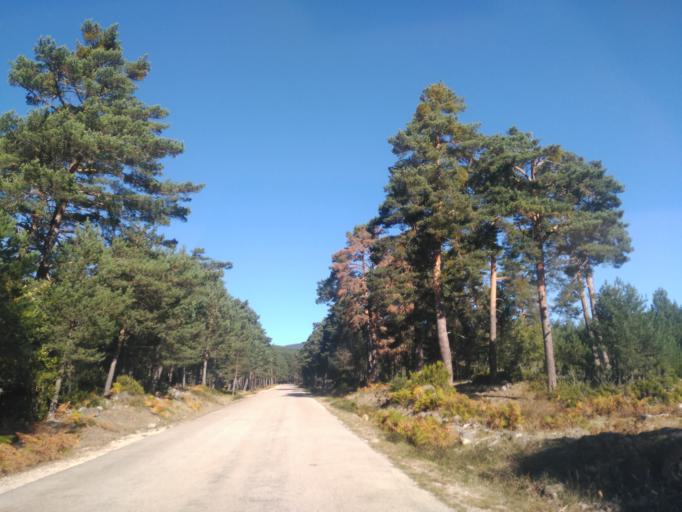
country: ES
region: Castille and Leon
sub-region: Provincia de Soria
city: Vinuesa
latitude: 41.9897
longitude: -2.7991
